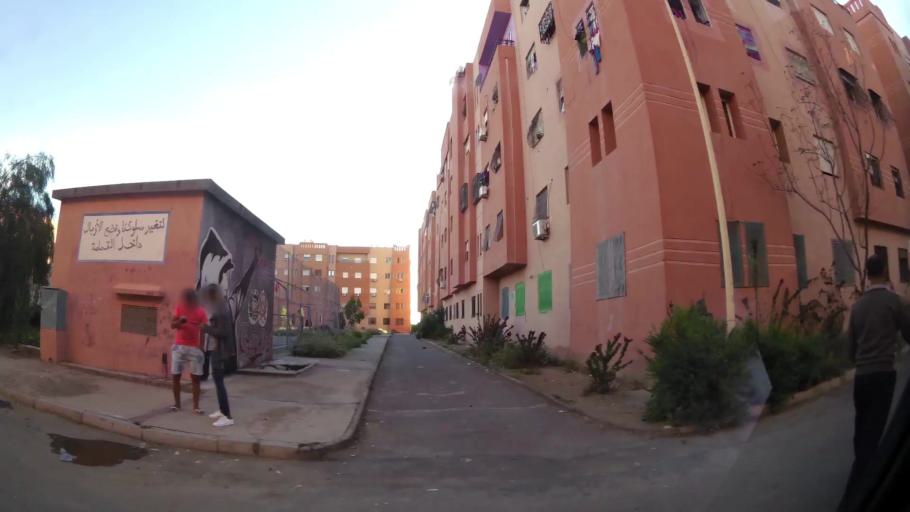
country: MA
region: Marrakech-Tensift-Al Haouz
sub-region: Marrakech
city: Marrakesh
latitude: 31.7492
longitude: -8.1187
